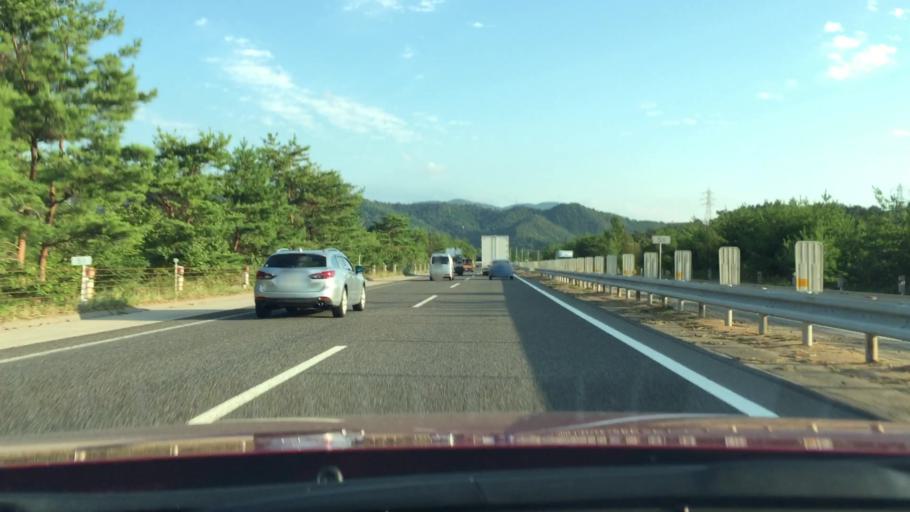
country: JP
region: Shiga Prefecture
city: Nagahama
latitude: 35.3642
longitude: 136.3062
